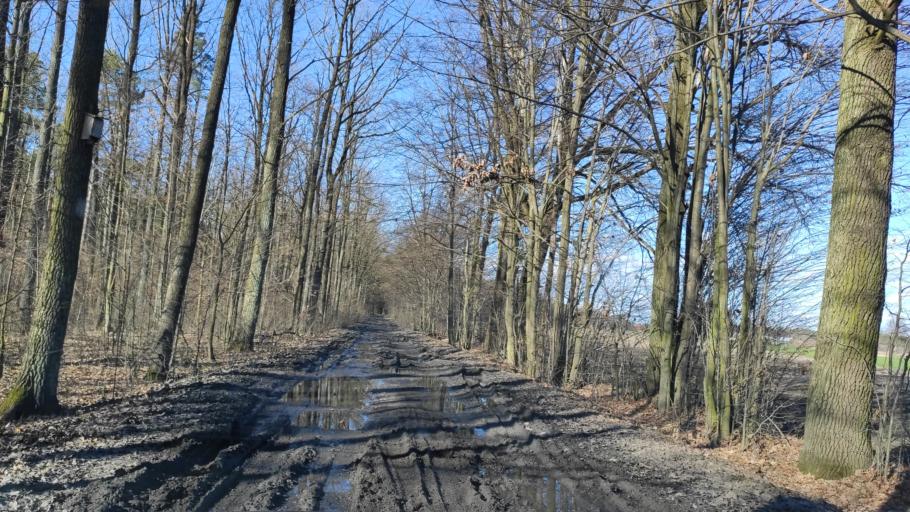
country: PL
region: Masovian Voivodeship
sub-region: Powiat radomski
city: Jedlnia-Letnisko
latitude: 51.4556
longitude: 21.3246
